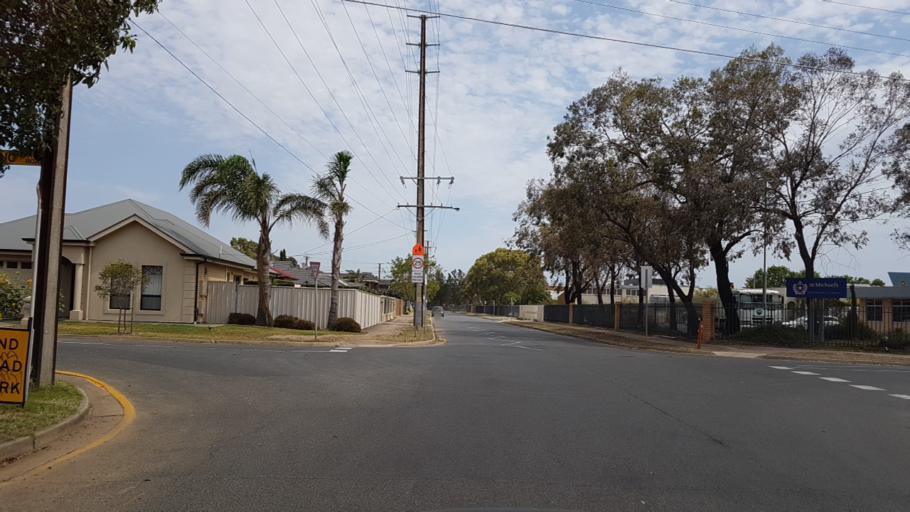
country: AU
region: South Australia
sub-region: Charles Sturt
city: Henley Beach
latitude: -34.9141
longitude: 138.5046
